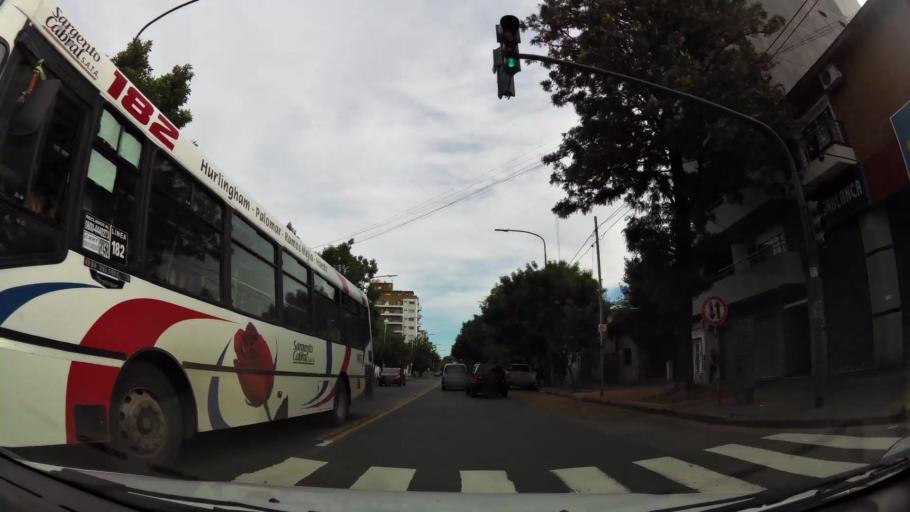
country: AR
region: Buenos Aires F.D.
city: Villa Santa Rita
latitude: -34.6366
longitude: -58.4873
